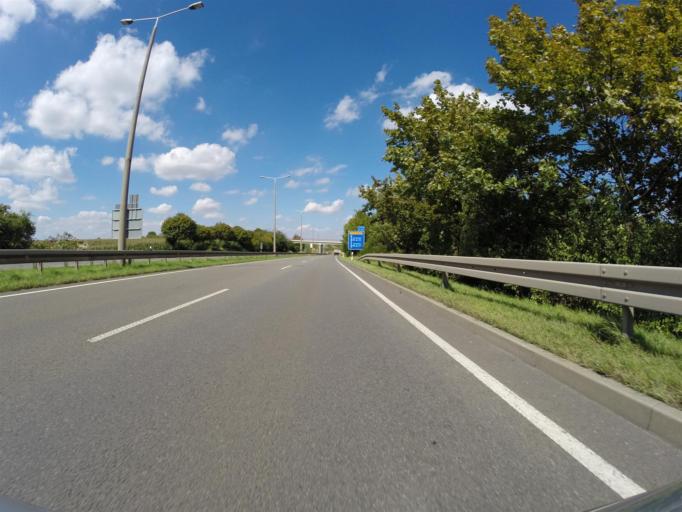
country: DE
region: Thuringia
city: Elxleben
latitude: 51.0159
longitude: 10.9836
